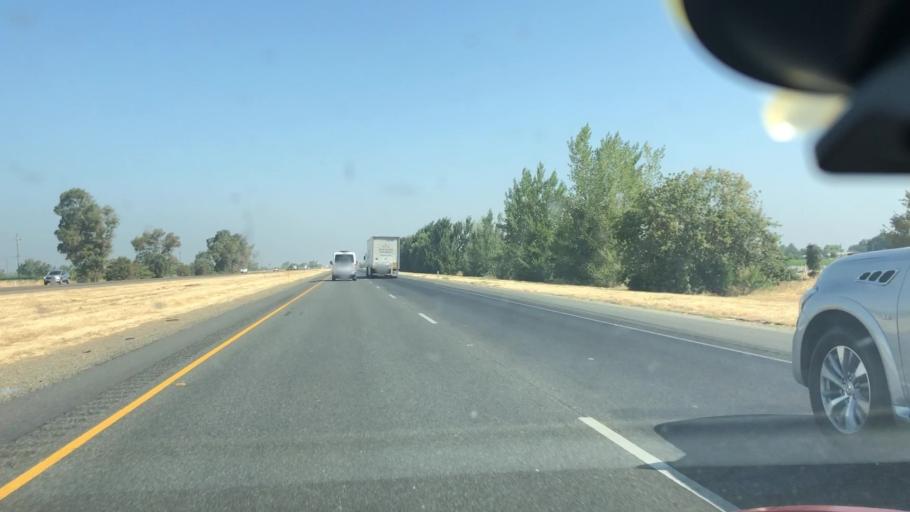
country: US
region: California
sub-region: Sacramento County
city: Laguna
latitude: 38.3320
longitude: -121.4676
